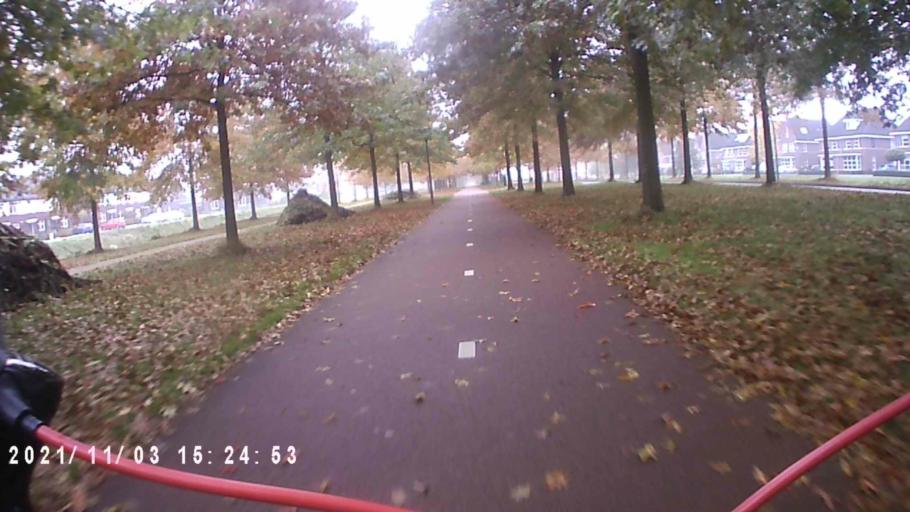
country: NL
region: Groningen
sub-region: Gemeente Leek
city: Leek
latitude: 53.1487
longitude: 6.3729
